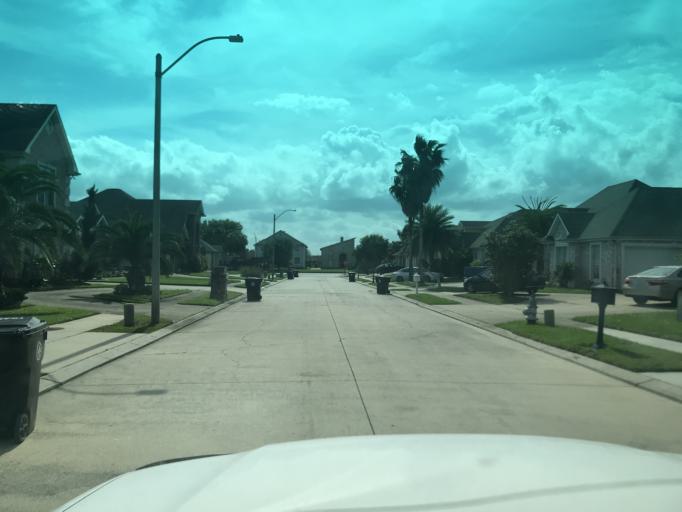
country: US
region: Louisiana
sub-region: Saint Bernard Parish
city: Chalmette
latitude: 30.0359
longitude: -89.9510
